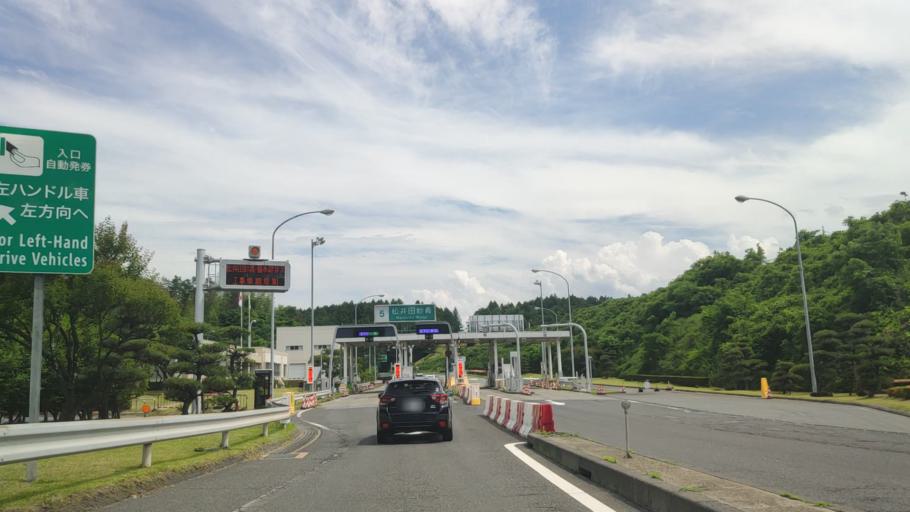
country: JP
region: Gunma
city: Annaka
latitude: 36.3141
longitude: 138.7733
